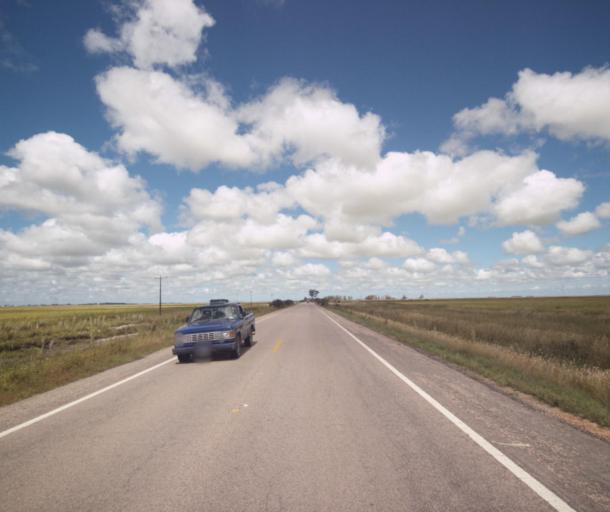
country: BR
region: Rio Grande do Sul
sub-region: Rio Grande
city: Rio Grande
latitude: -32.1689
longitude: -52.4106
